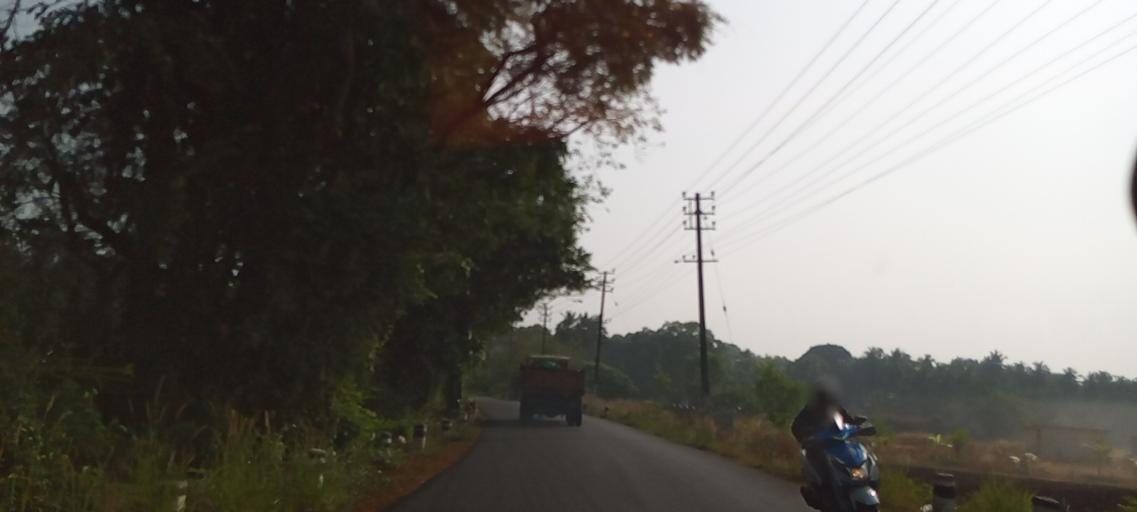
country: IN
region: Karnataka
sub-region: Udupi
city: Coondapoor
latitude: 13.5078
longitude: 74.7245
